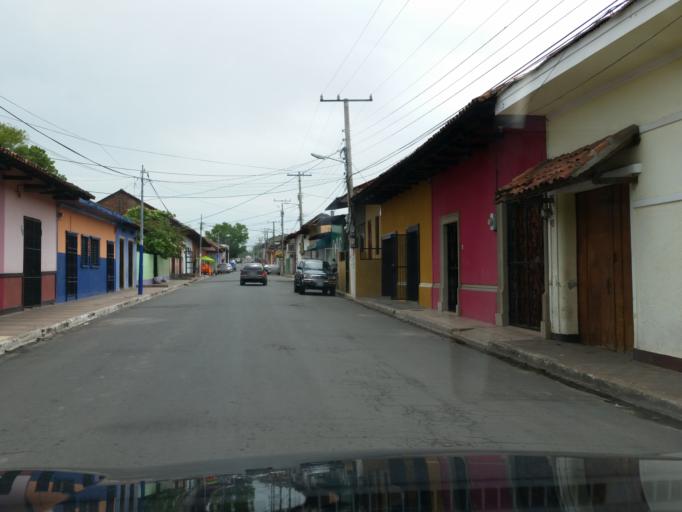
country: NI
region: Granada
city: Granada
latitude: 11.9308
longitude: -85.9592
